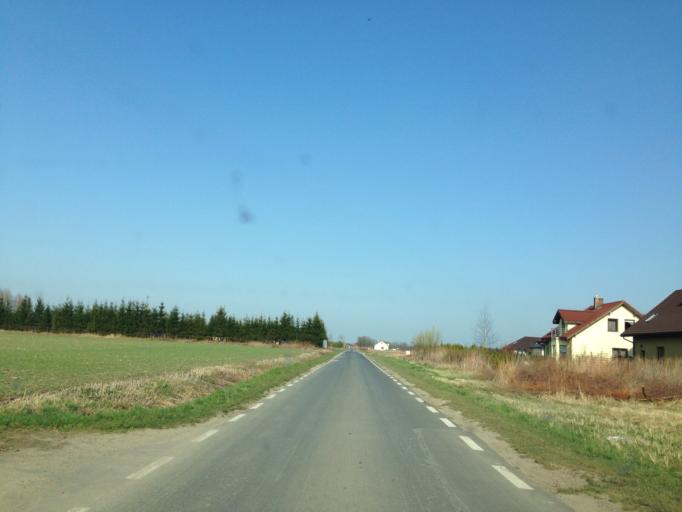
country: PL
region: Lower Silesian Voivodeship
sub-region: Powiat wroclawski
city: Kamieniec Wroclawski
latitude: 51.0960
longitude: 17.2026
